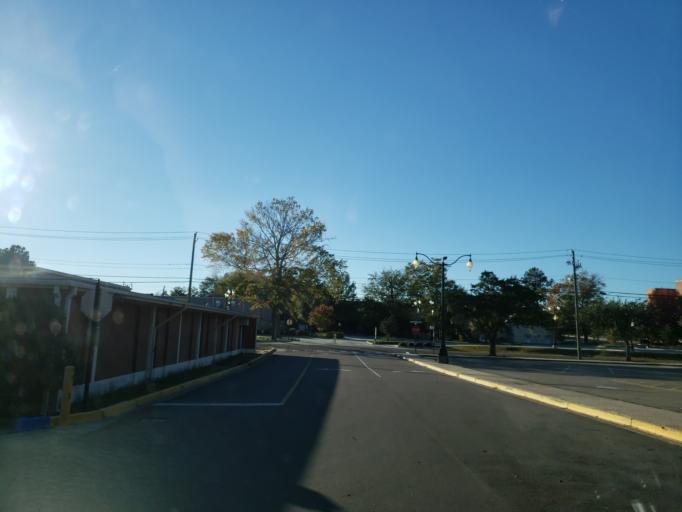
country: US
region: Mississippi
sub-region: Lamar County
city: Arnold Line
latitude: 31.3260
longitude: -89.3353
